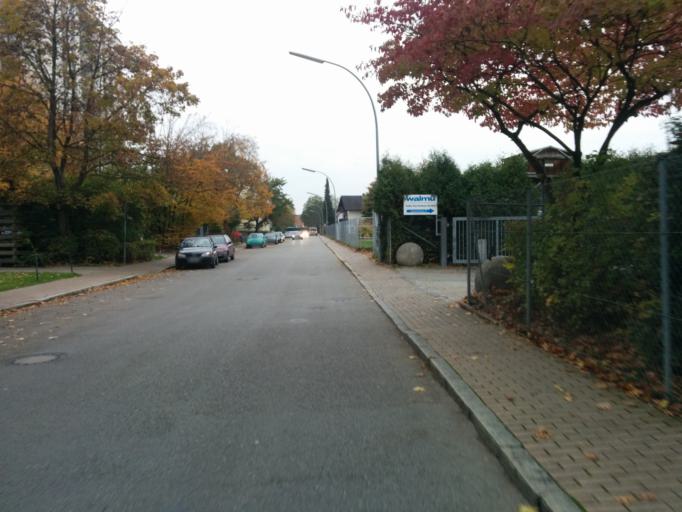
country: DE
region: Bavaria
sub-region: Upper Bavaria
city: Freising
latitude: 48.3956
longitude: 11.7687
